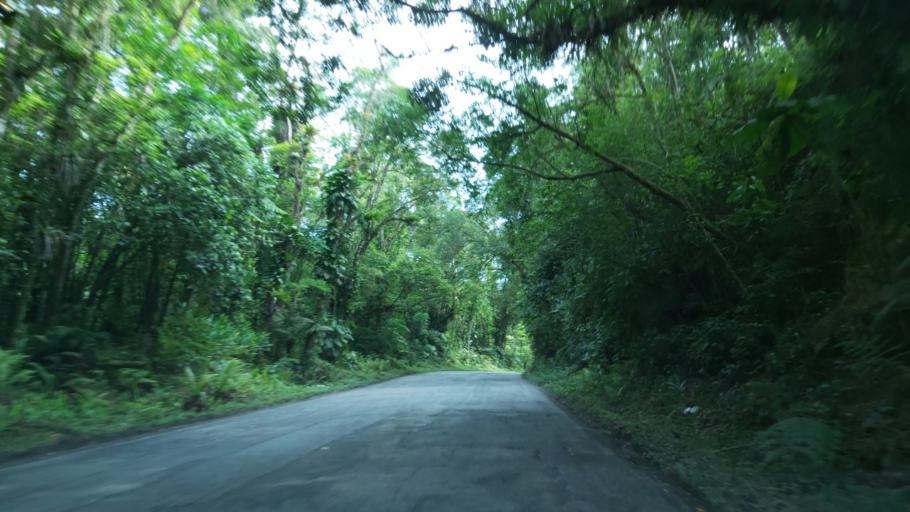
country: BR
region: Sao Paulo
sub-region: Miracatu
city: Miracatu
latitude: -24.0577
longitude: -47.5871
